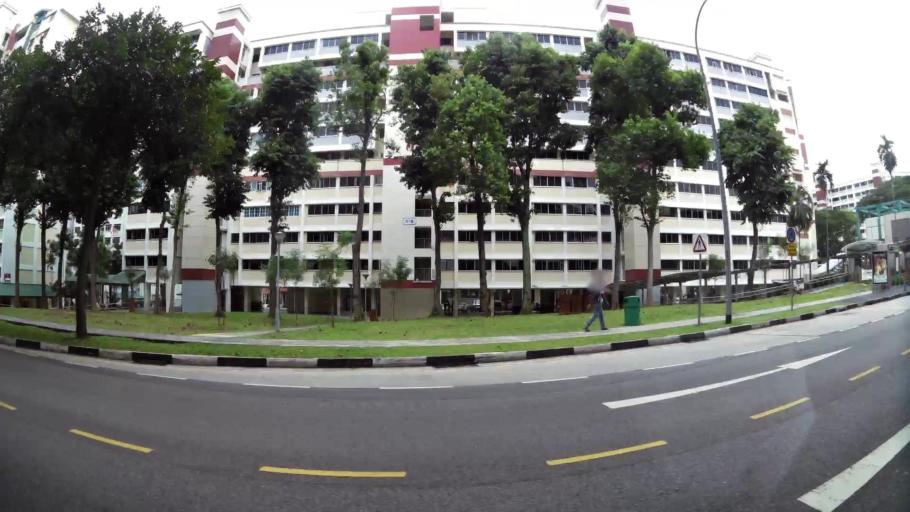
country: SG
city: Singapore
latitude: 1.3506
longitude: 103.8746
